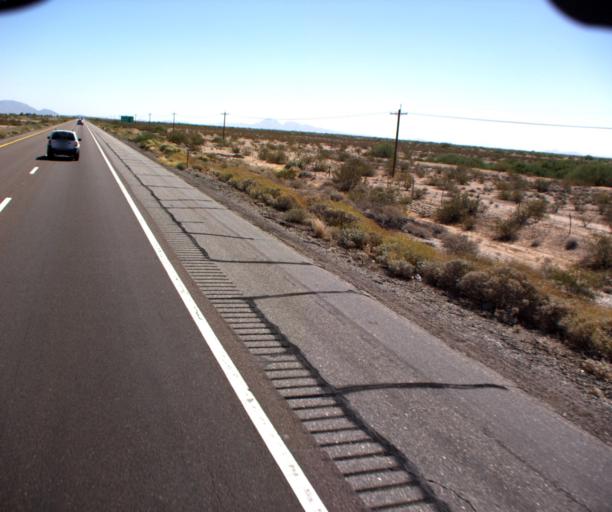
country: US
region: Arizona
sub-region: La Paz County
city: Salome
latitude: 33.5656
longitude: -113.3327
